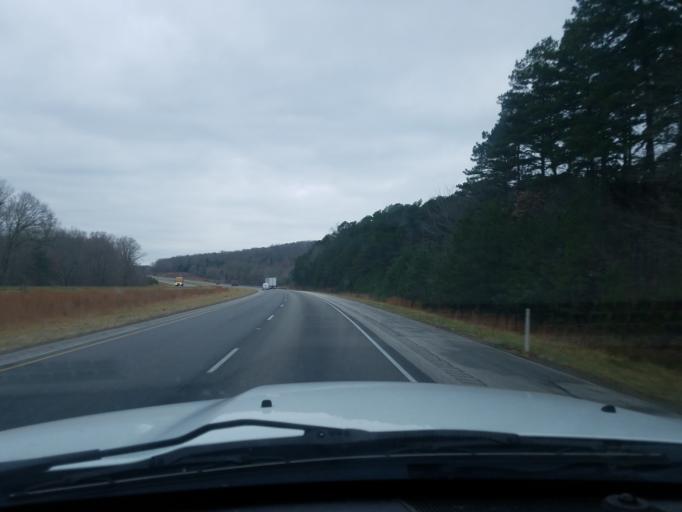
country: US
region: Indiana
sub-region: Crawford County
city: English
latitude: 38.2413
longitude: -86.5467
